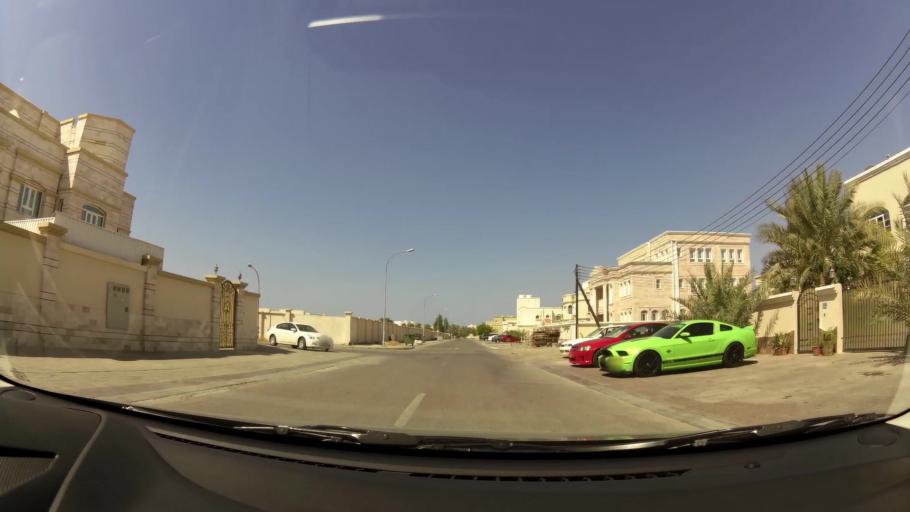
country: OM
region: Muhafazat Masqat
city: As Sib al Jadidah
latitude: 23.6353
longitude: 58.2150
